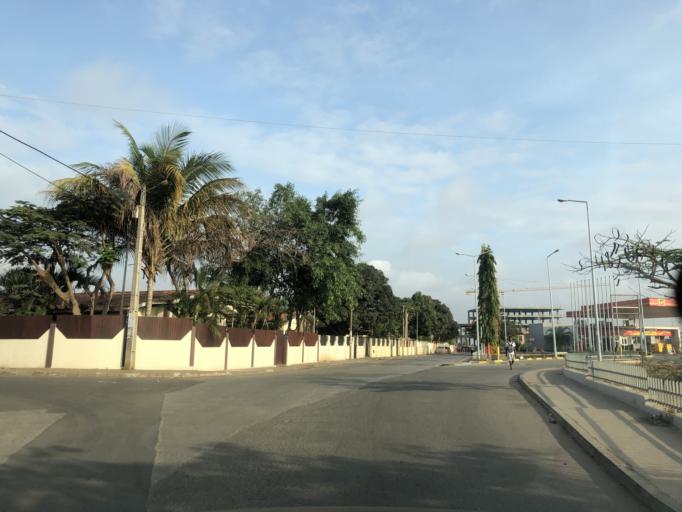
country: AO
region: Luanda
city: Luanda
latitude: -8.8981
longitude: 13.2288
